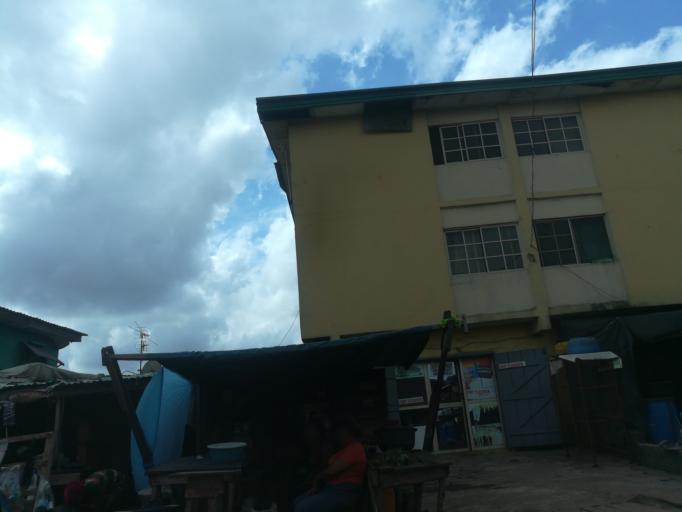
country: NG
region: Lagos
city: Somolu
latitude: 6.5406
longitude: 3.3612
